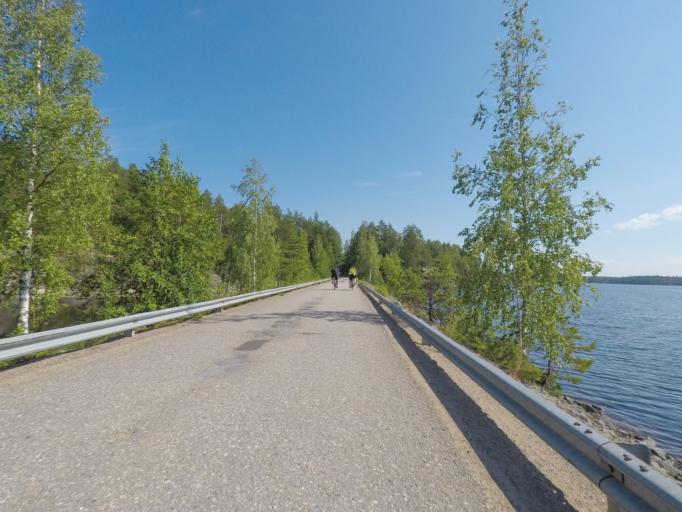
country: FI
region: Southern Savonia
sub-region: Mikkeli
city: Puumala
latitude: 61.4059
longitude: 28.0653
